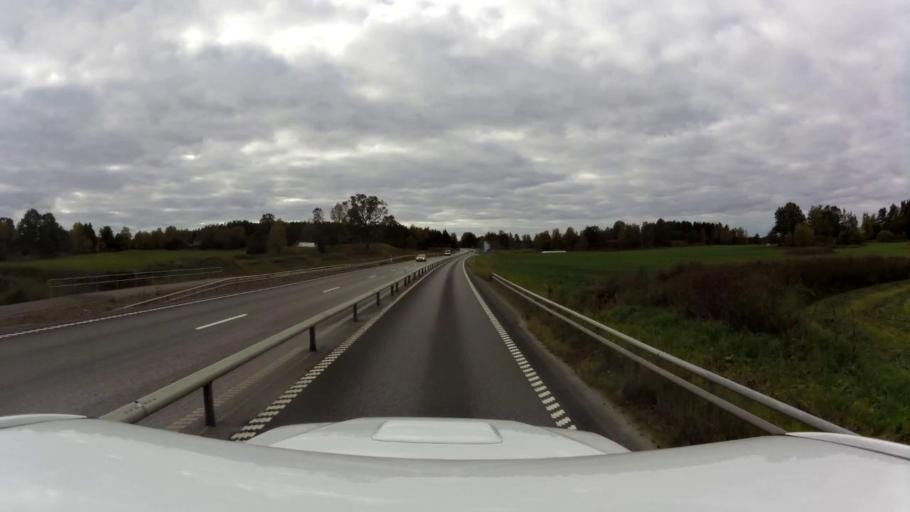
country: SE
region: OEstergoetland
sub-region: Linkopings Kommun
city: Malmslatt
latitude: 58.3082
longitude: 15.5662
